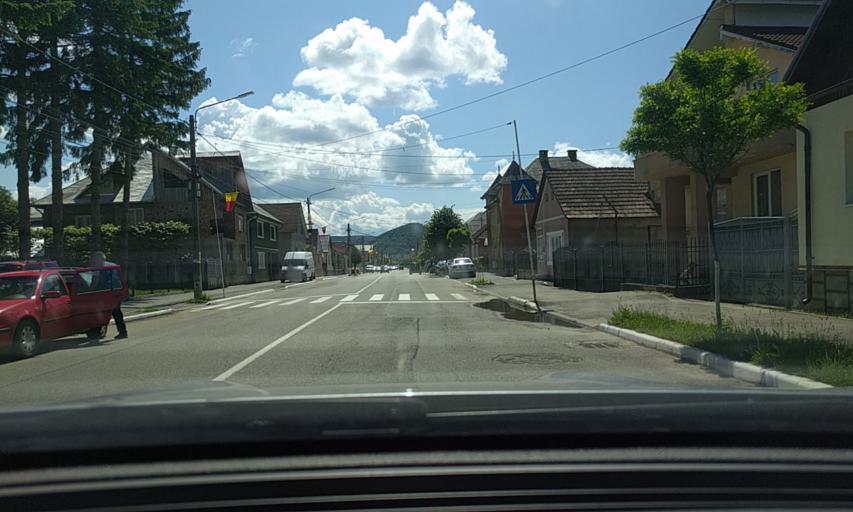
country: RO
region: Bistrita-Nasaud
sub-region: Oras Nasaud
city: Nasaud
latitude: 47.2921
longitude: 24.3878
